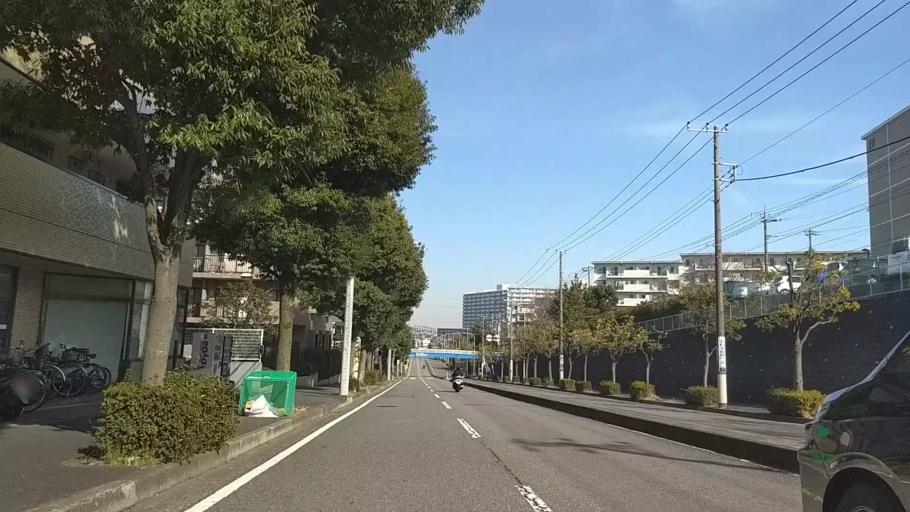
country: JP
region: Kanagawa
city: Kamakura
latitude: 35.3700
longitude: 139.5830
